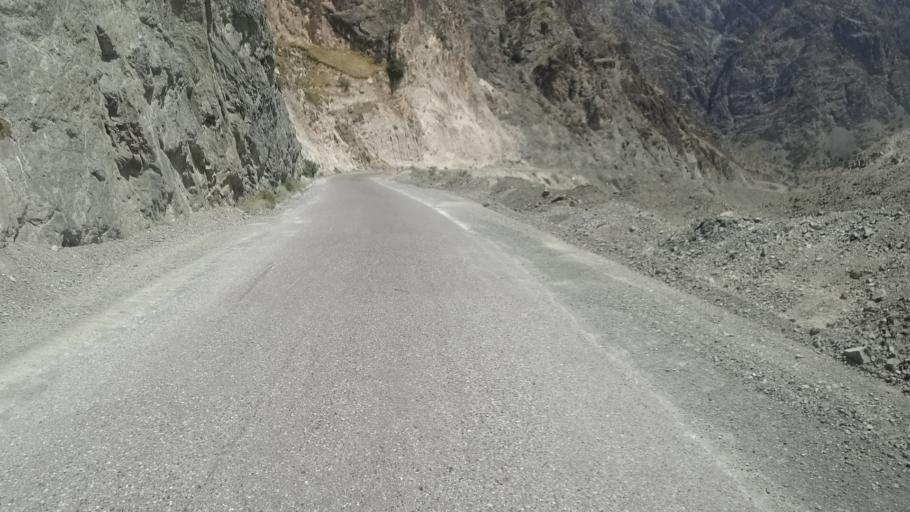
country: AF
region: Badakhshan
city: Deh Khwahan
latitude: 37.9744
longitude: 70.2747
